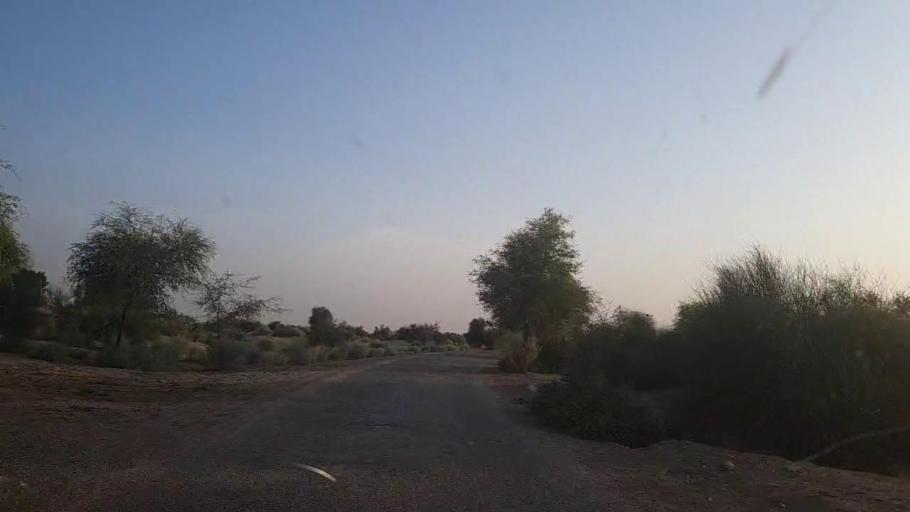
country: PK
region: Sindh
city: Khanpur
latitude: 27.6038
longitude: 69.4334
